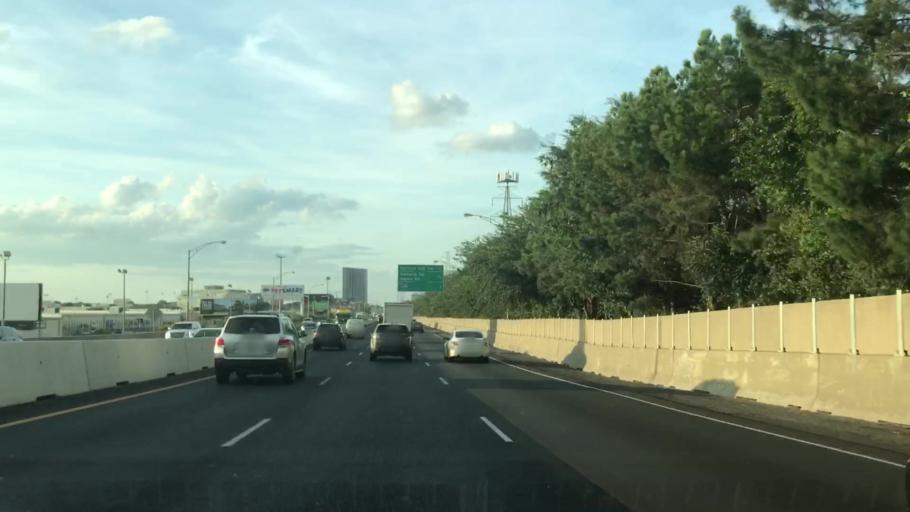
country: US
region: Texas
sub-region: Dallas County
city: Addison
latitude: 32.9103
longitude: -96.8147
